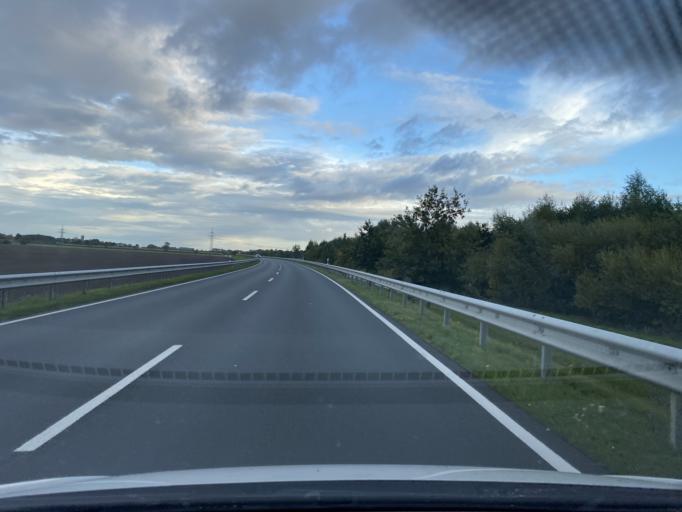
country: DE
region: Lower Saxony
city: Otterndorf
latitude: 53.7971
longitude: 8.8765
